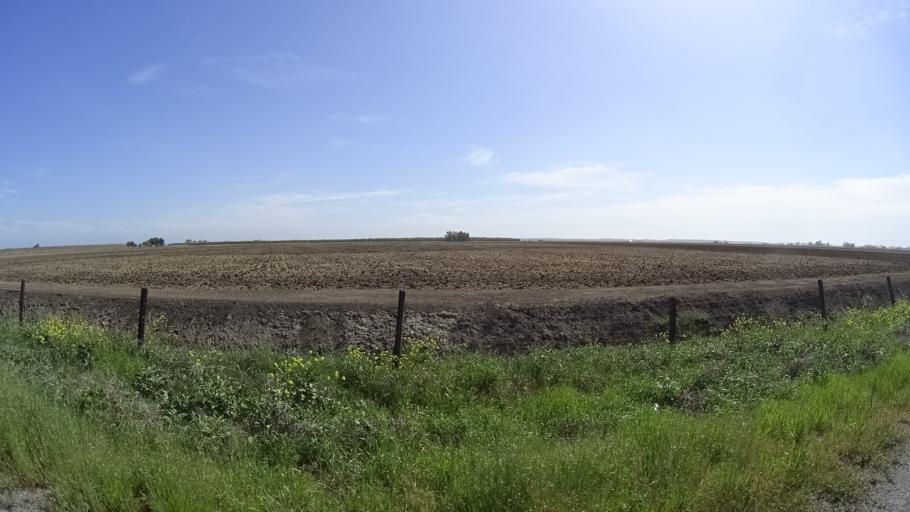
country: US
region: California
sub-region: Glenn County
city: Hamilton City
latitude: 39.6104
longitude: -122.0557
